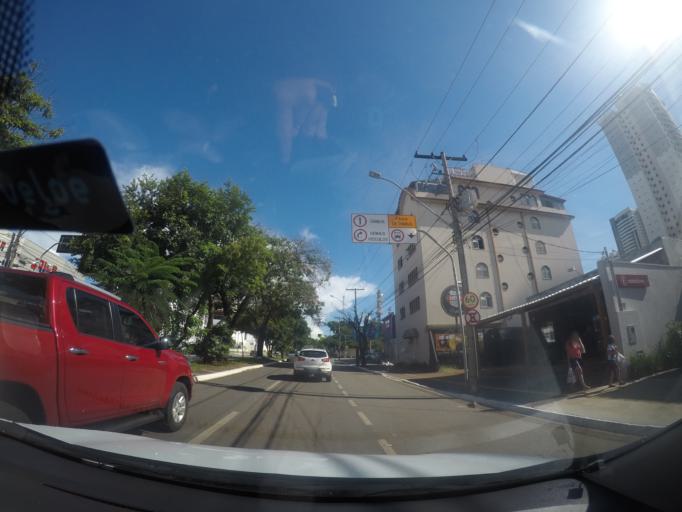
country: BR
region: Goias
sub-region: Goiania
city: Goiania
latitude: -16.7195
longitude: -49.2635
